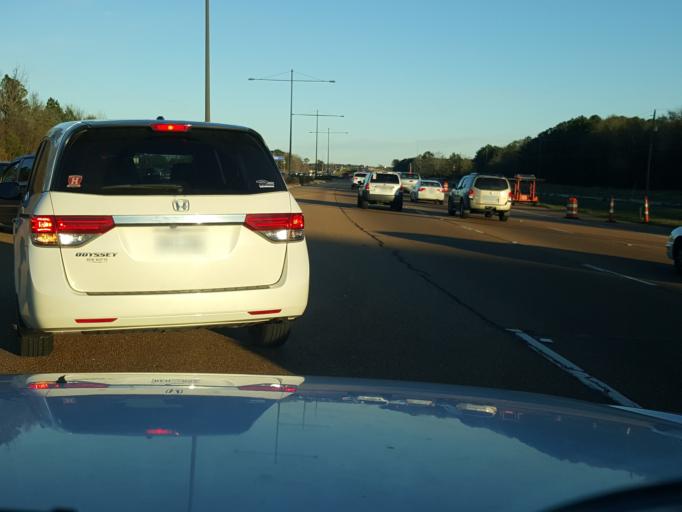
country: US
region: Mississippi
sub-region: Rankin County
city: Flowood
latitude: 32.3396
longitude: -90.0876
